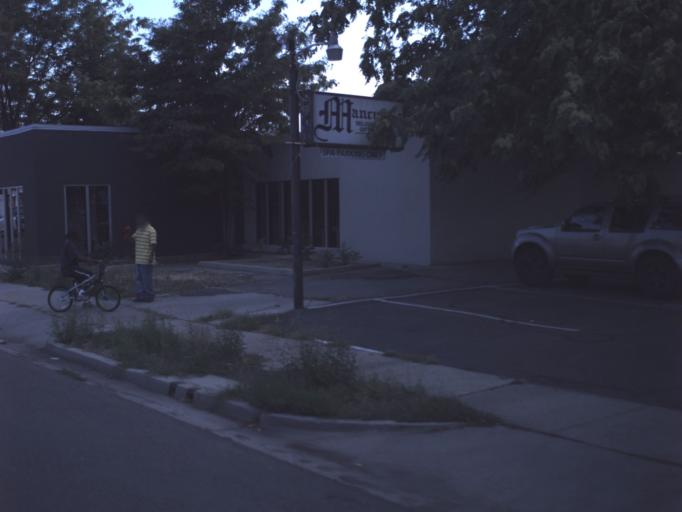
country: US
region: Utah
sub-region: Salt Lake County
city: South Salt Lake
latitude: 40.7312
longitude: -111.8884
